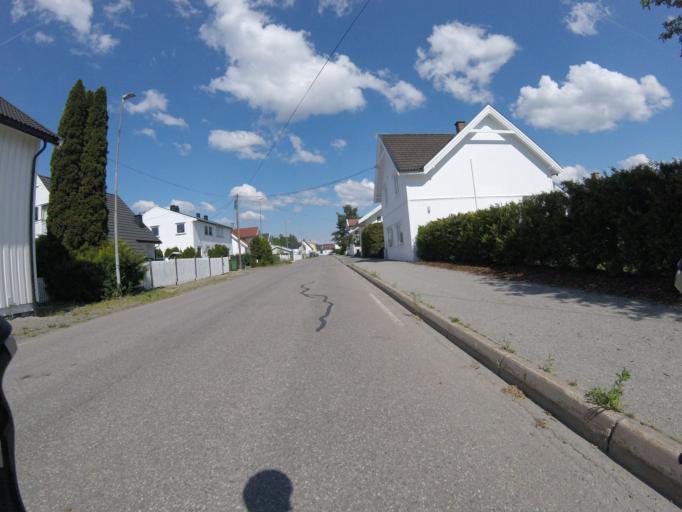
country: NO
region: Akershus
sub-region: Skedsmo
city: Lillestrom
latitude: 59.9499
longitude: 11.0610
